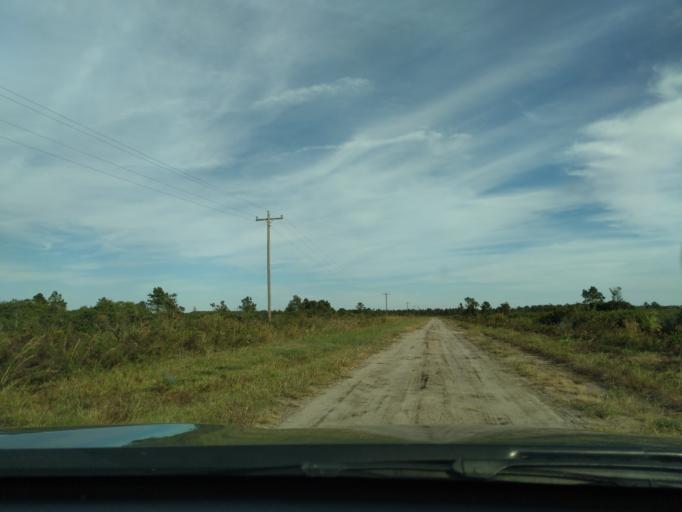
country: US
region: North Carolina
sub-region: Beaufort County
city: Belhaven
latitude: 35.6898
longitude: -76.5317
